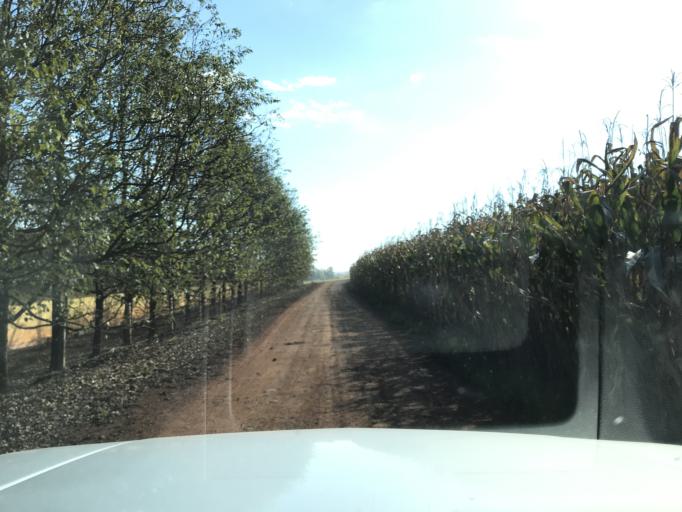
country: BR
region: Parana
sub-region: Palotina
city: Palotina
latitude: -24.2677
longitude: -53.8148
